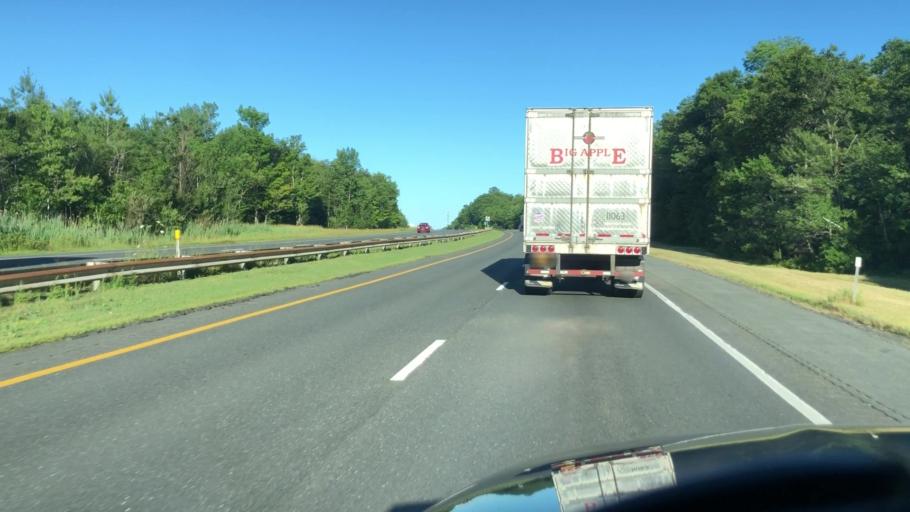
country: US
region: Massachusetts
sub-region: Berkshire County
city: Otis
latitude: 42.2362
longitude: -73.0216
